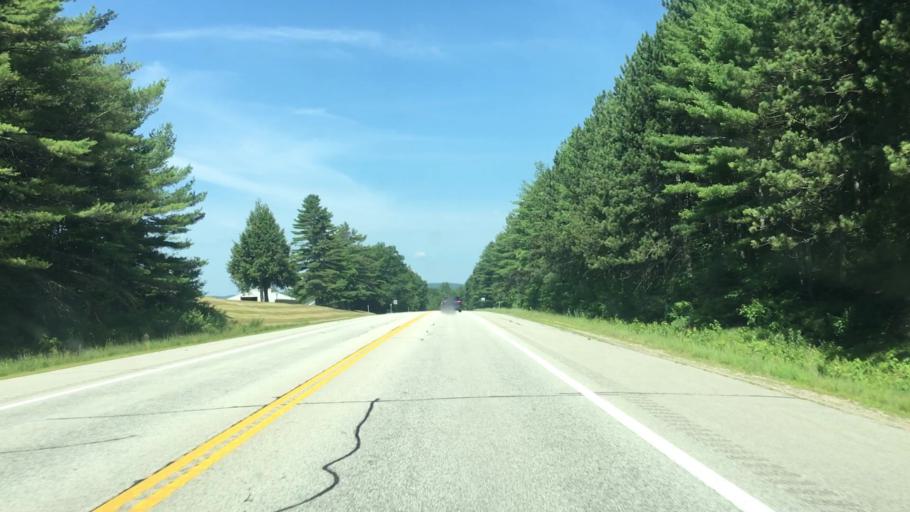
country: US
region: New Hampshire
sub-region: Merrimack County
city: Henniker
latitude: 43.1818
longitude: -71.7716
